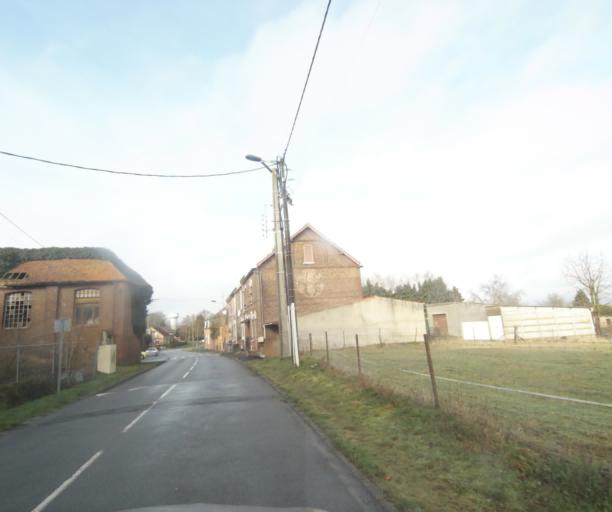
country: FR
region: Nord-Pas-de-Calais
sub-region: Departement du Nord
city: Artres
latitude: 50.2855
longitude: 3.5488
